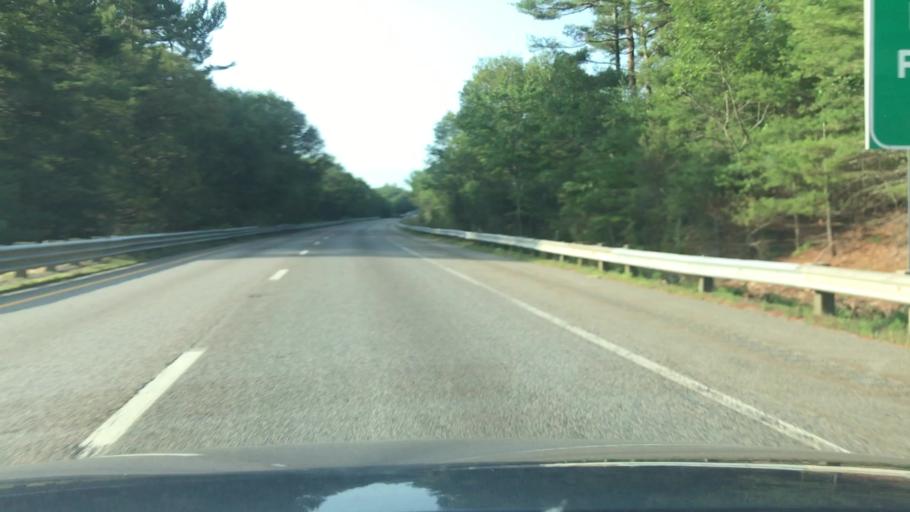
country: US
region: Massachusetts
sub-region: Plymouth County
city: Marshfield
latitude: 42.0647
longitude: -70.7282
